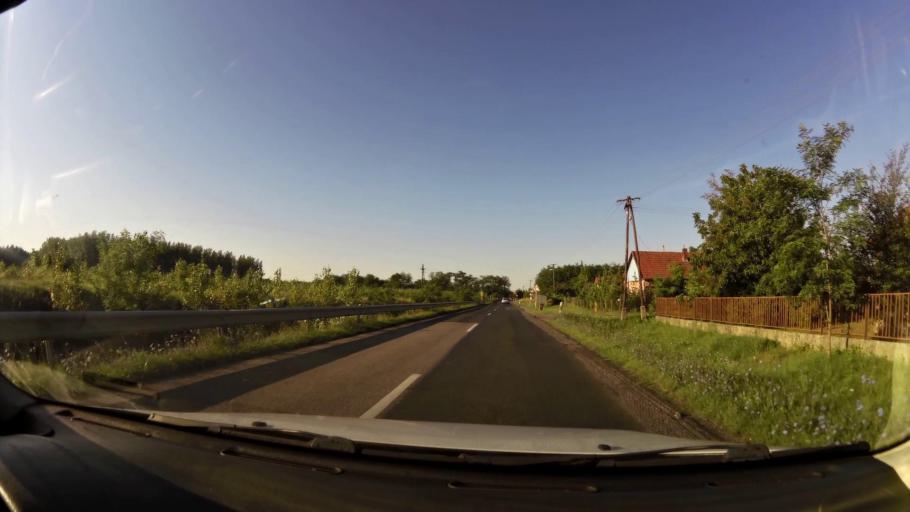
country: HU
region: Pest
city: Tapioszolos
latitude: 47.2756
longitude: 19.8653
